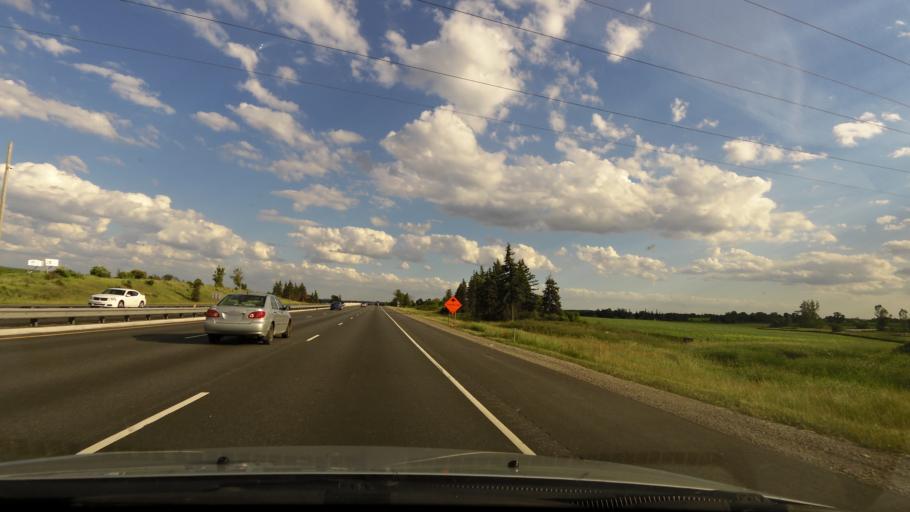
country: CA
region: Ontario
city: Bradford West Gwillimbury
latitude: 44.0873
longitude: -79.6280
